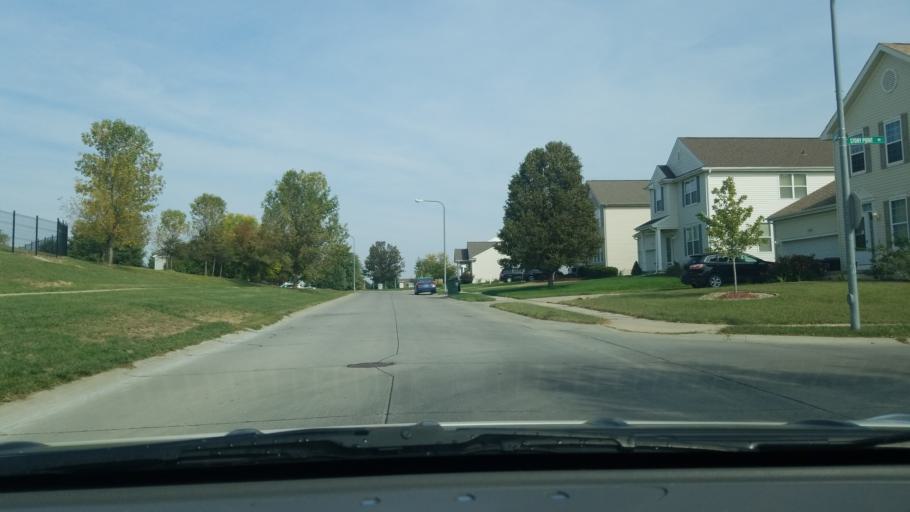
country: US
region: Nebraska
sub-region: Sarpy County
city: Papillion
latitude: 41.1293
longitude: -96.0555
